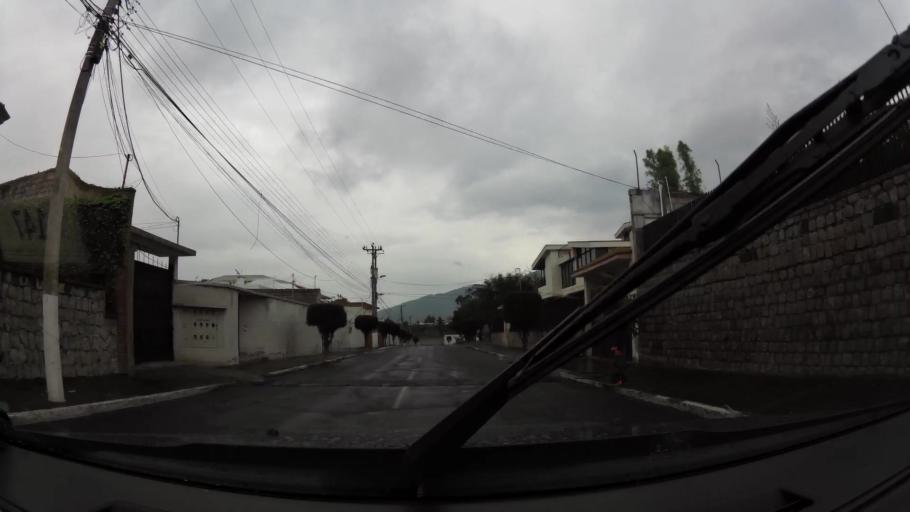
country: EC
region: Pichincha
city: Sangolqui
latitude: -0.3134
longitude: -78.4413
